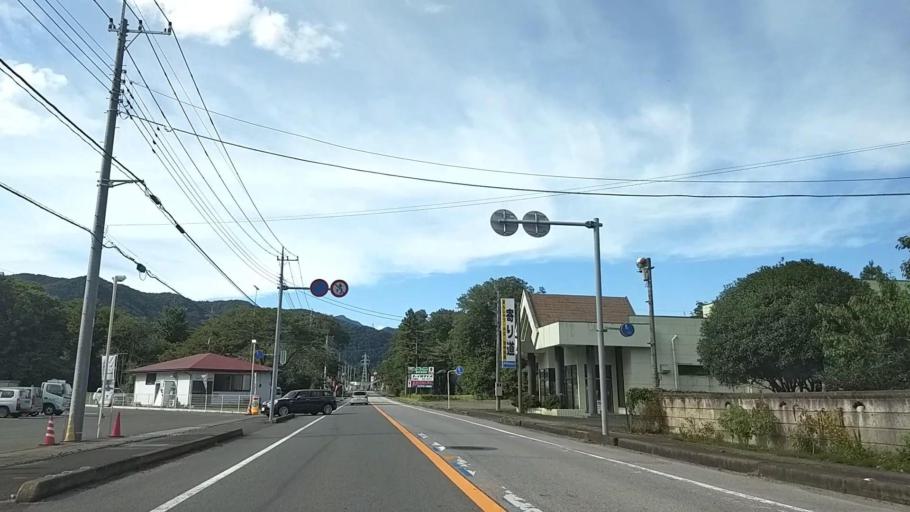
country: JP
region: Tochigi
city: Imaichi
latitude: 36.7803
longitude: 139.7051
